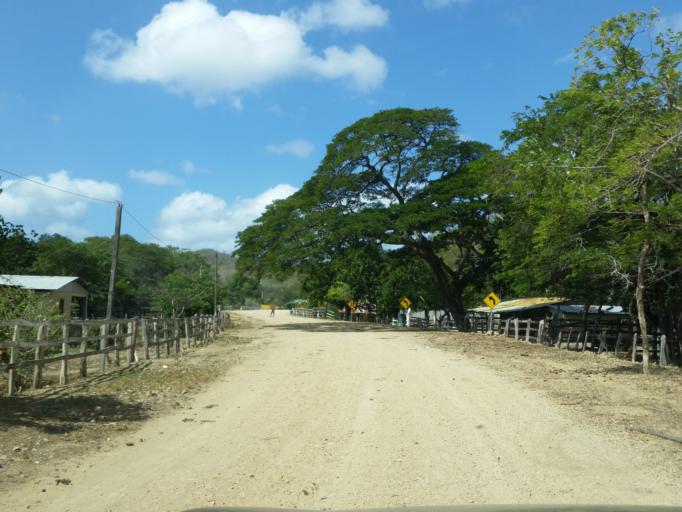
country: CR
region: Guanacaste
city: La Cruz
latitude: 11.1119
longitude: -85.7575
